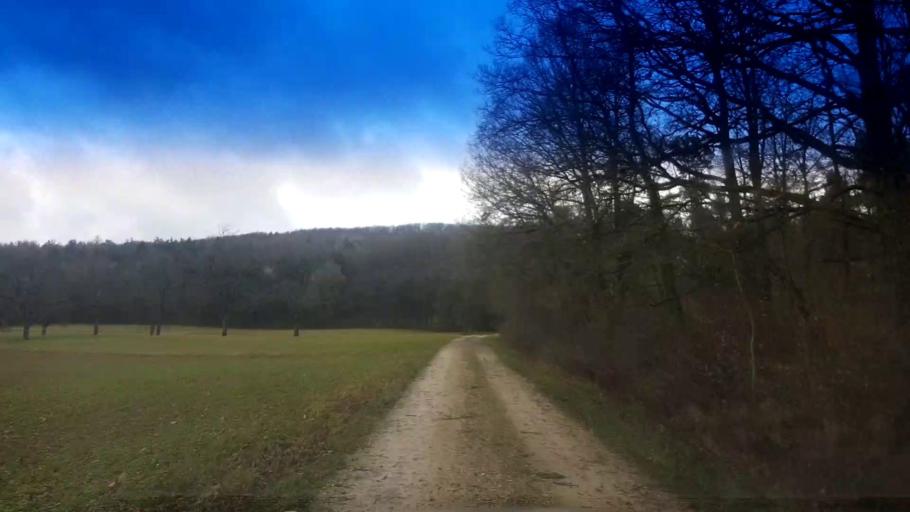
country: DE
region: Bavaria
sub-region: Upper Franconia
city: Schesslitz
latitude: 49.9441
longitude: 11.0324
